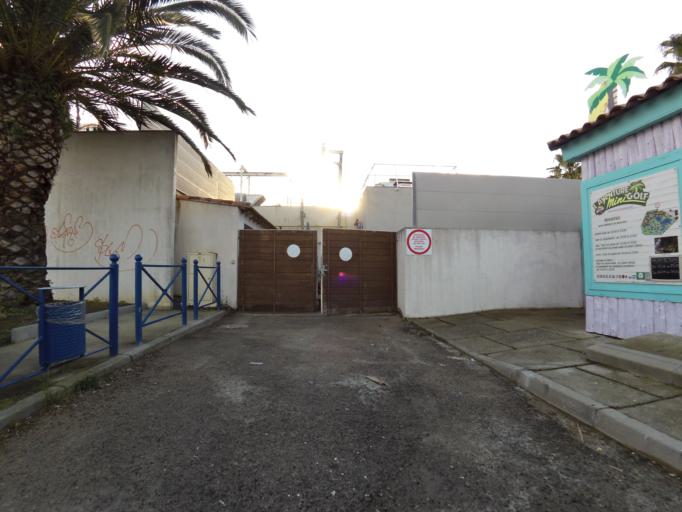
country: FR
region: Languedoc-Roussillon
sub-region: Departement du Gard
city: Le Grau-du-Roi
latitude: 43.5277
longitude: 4.1410
